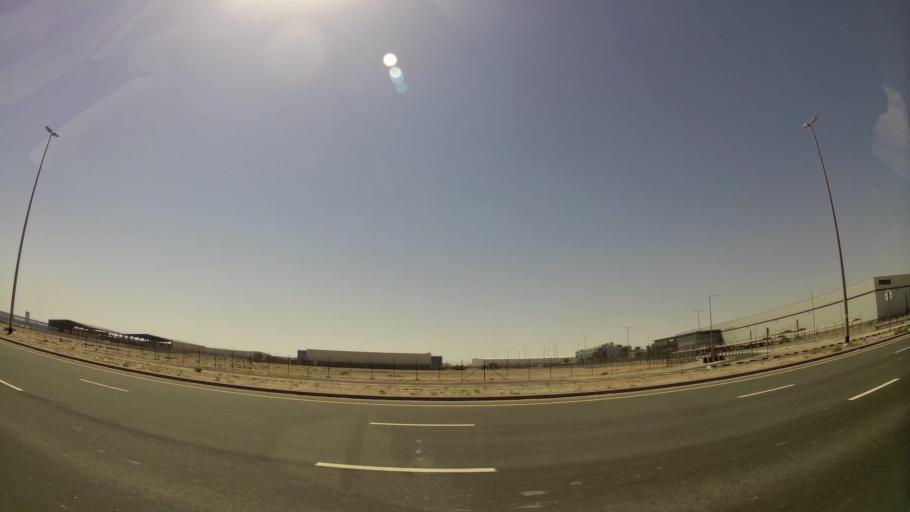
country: AE
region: Dubai
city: Dubai
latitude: 24.9664
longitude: 55.1255
